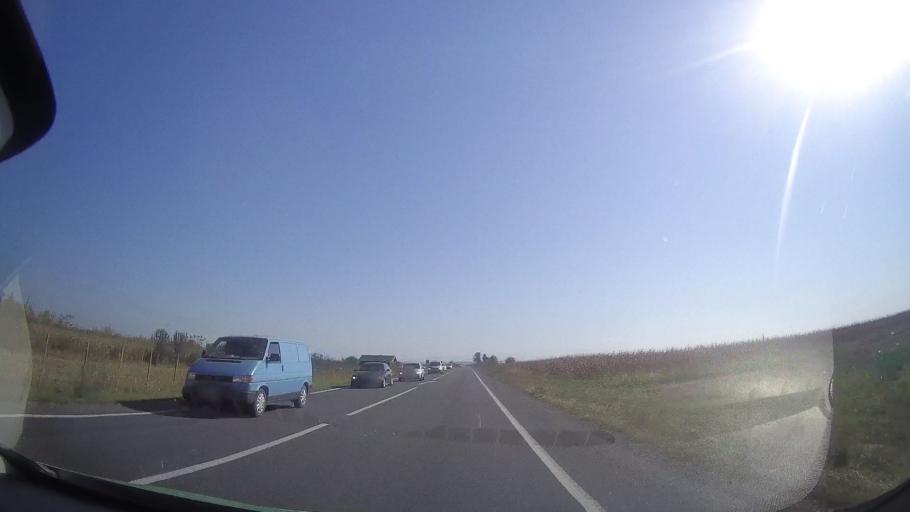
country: RO
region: Timis
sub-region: Comuna Belint
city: Belint
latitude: 45.7469
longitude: 21.7896
